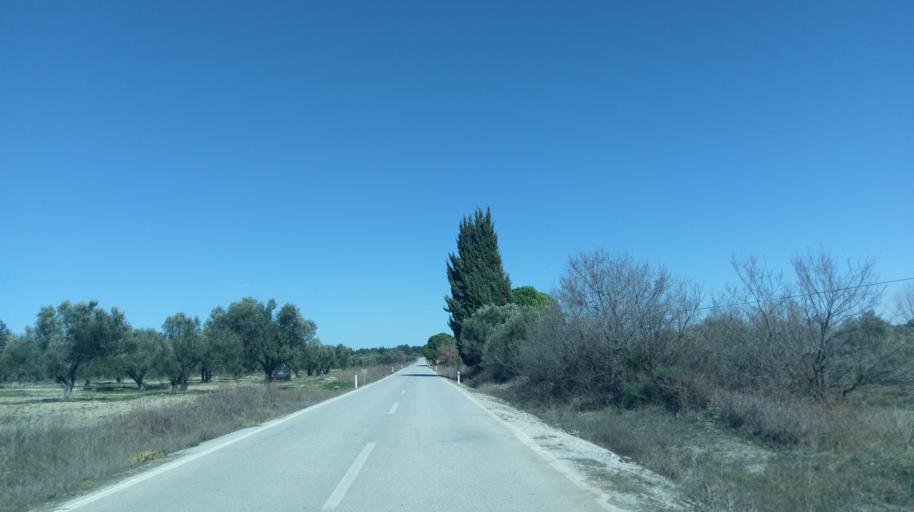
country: TR
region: Canakkale
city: Intepe
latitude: 40.0700
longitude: 26.2084
